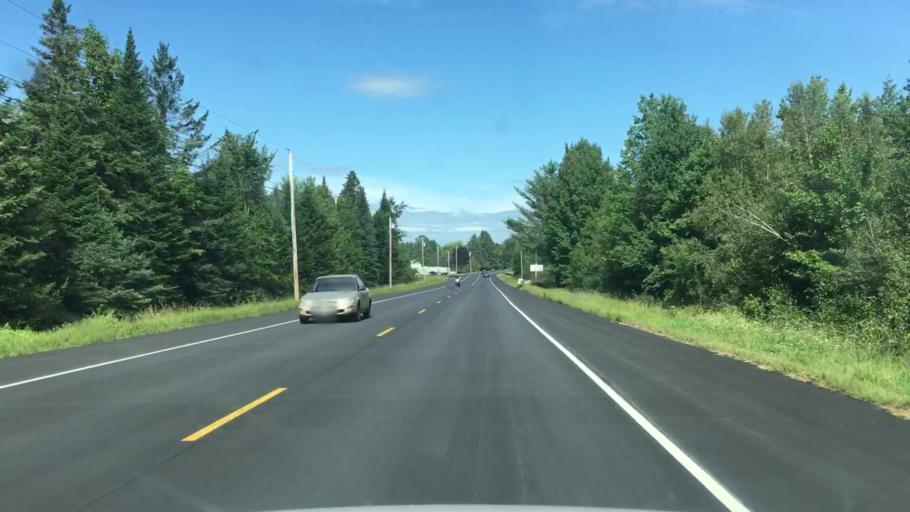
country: US
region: Maine
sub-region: Penobscot County
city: Corinna
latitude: 44.9658
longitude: -69.2726
